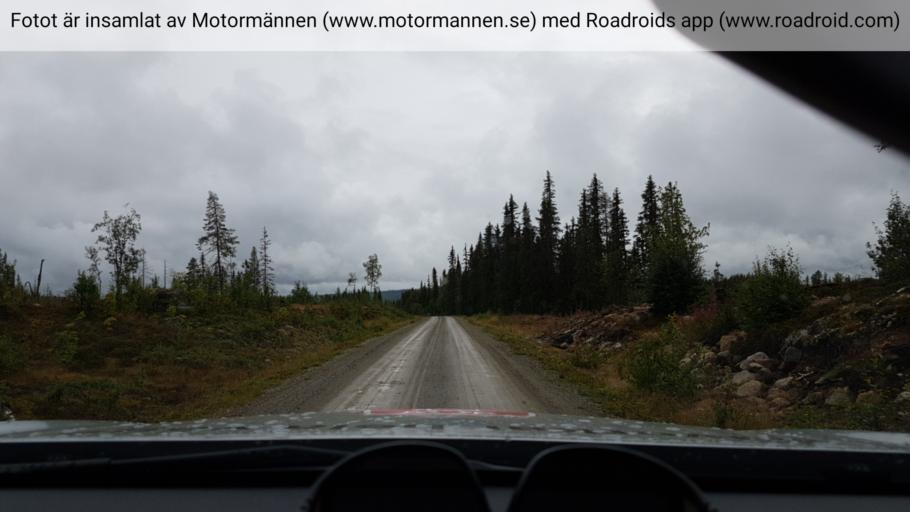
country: SE
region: Vaesterbotten
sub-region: Storumans Kommun
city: Storuman
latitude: 64.8448
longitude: 17.4085
